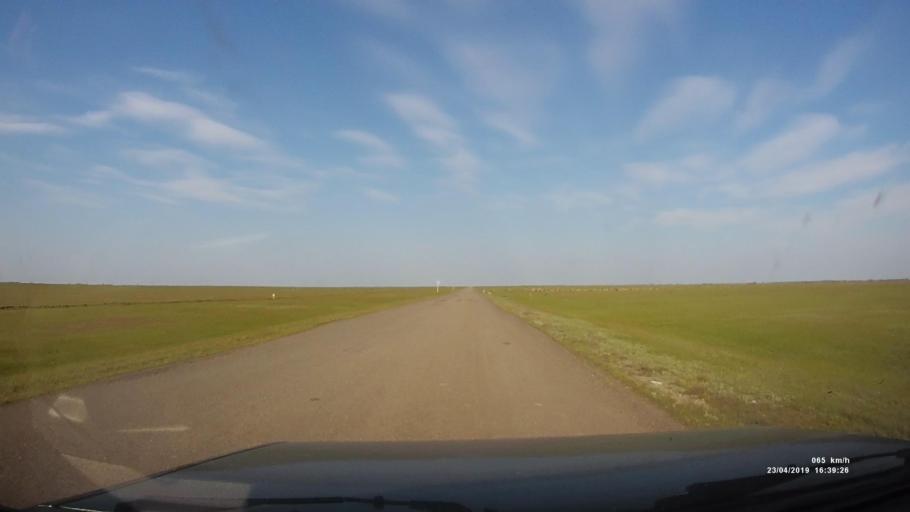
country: RU
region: Kalmykiya
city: Priyutnoye
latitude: 46.3396
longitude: 43.1659
